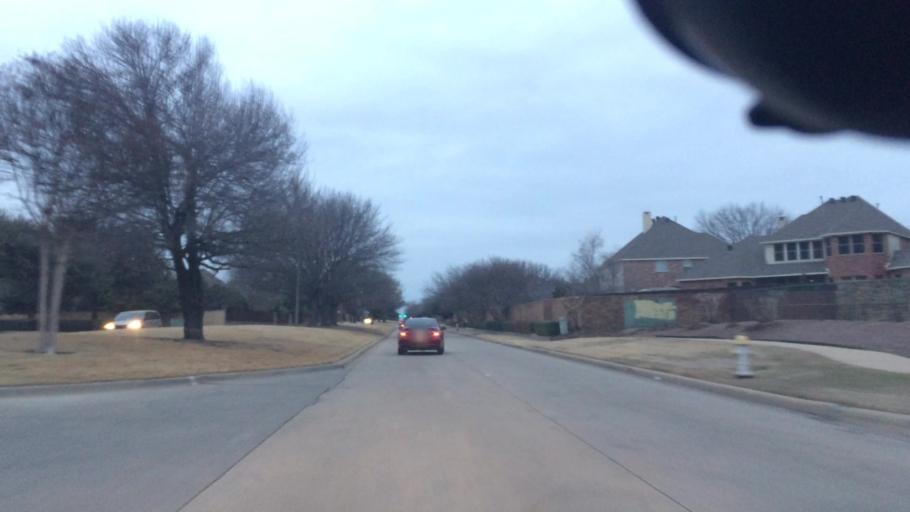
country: US
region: Texas
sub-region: Collin County
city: Allen
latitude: 33.1020
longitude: -96.6983
